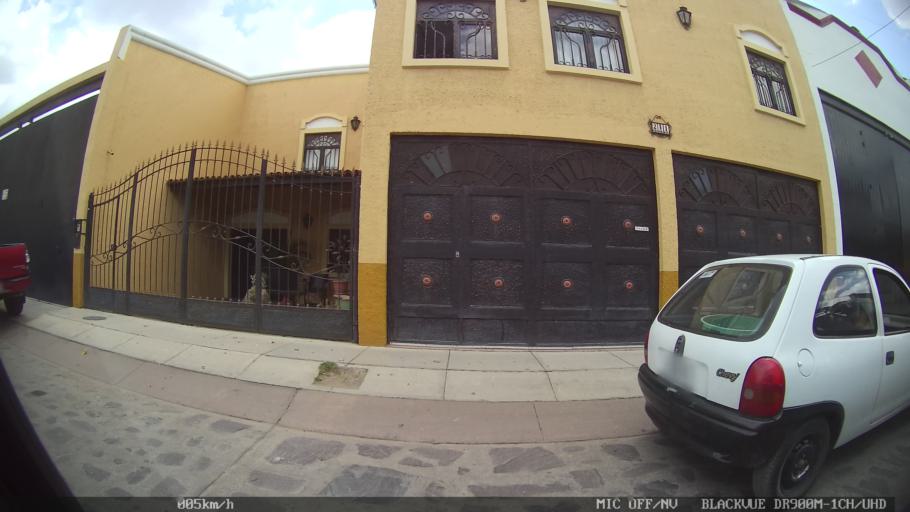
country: MX
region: Jalisco
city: Tonala
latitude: 20.6532
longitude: -103.2325
